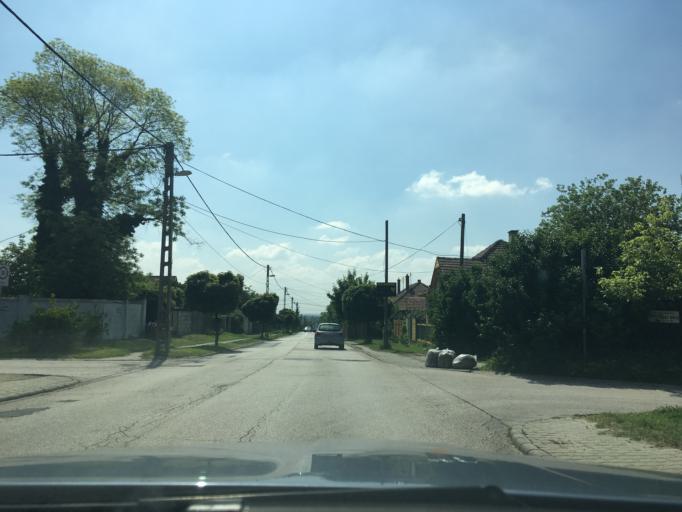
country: HU
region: Budapest
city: Budapest XXII. keruelet
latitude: 47.4171
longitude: 19.0185
